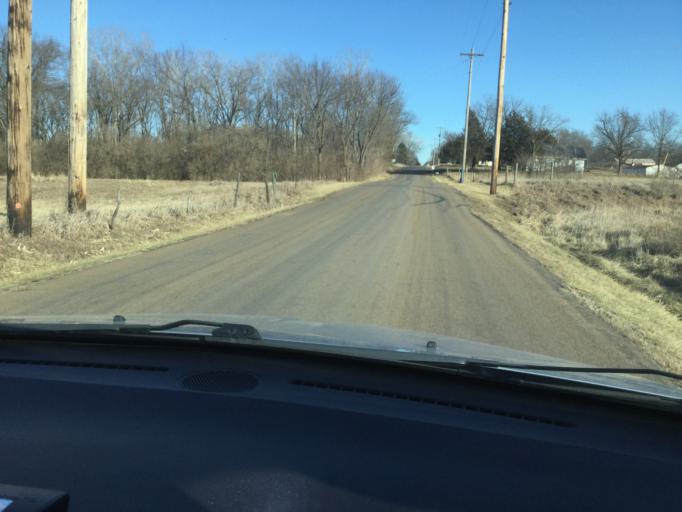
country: US
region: Kansas
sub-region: Shawnee County
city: Topeka
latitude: 39.1165
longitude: -95.6988
